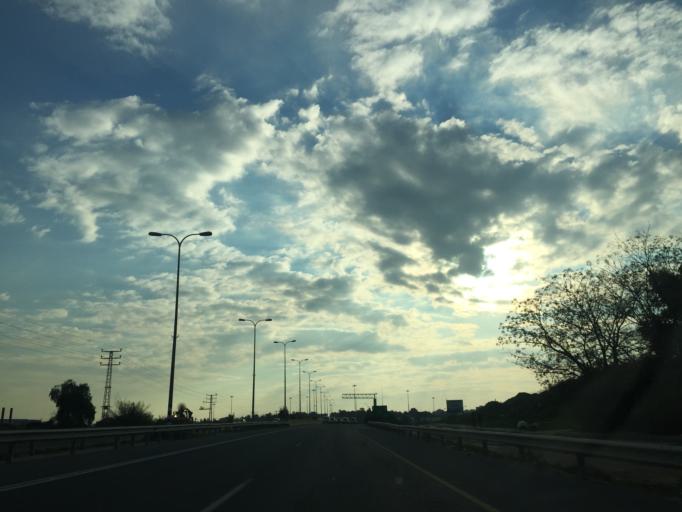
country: IL
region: Central District
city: Lod
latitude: 31.9290
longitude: 34.8887
